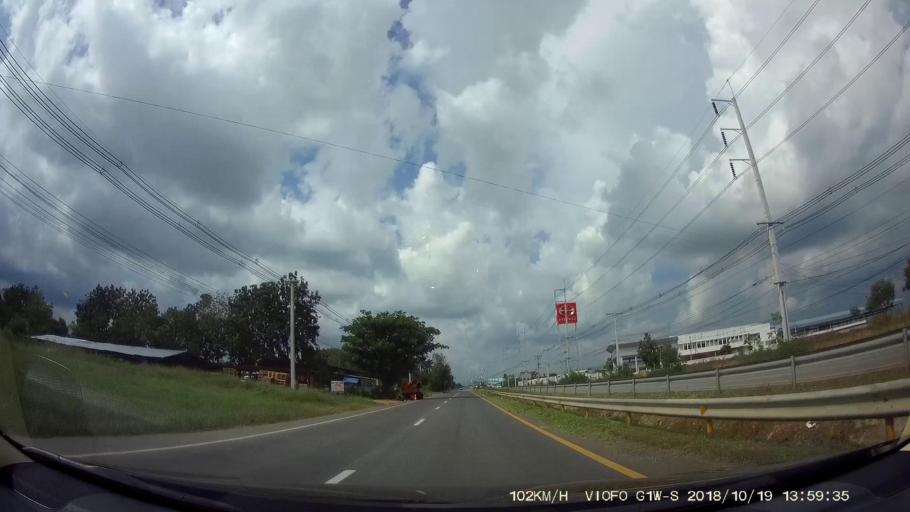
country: TH
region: Chaiyaphum
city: Chaiyaphum
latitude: 15.8118
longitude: 102.0606
